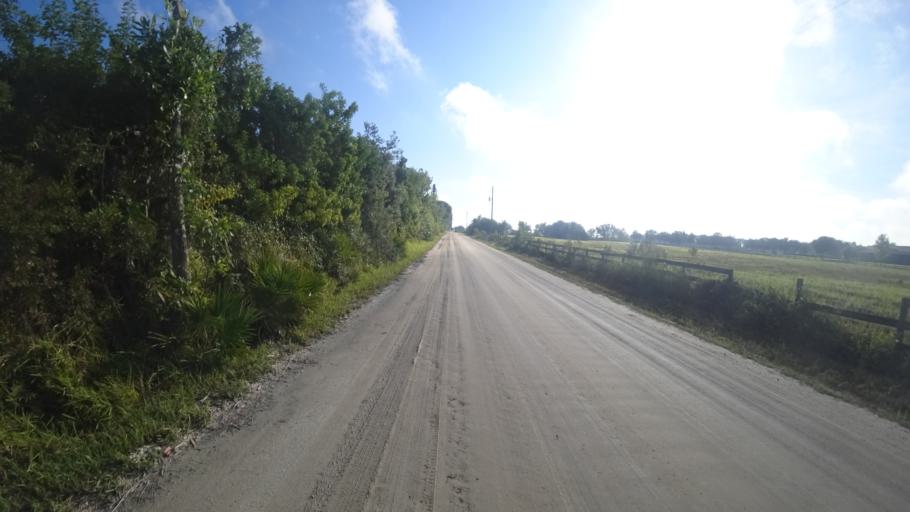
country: US
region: Florida
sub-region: Sarasota County
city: The Meadows
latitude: 27.4310
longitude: -82.3056
